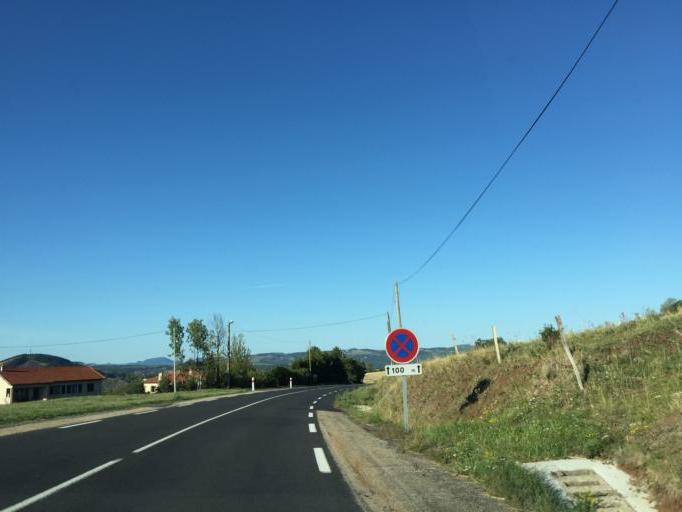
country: FR
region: Auvergne
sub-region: Departement de la Haute-Loire
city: Espaly-Saint-Marcel
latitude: 45.0299
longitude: 3.8450
